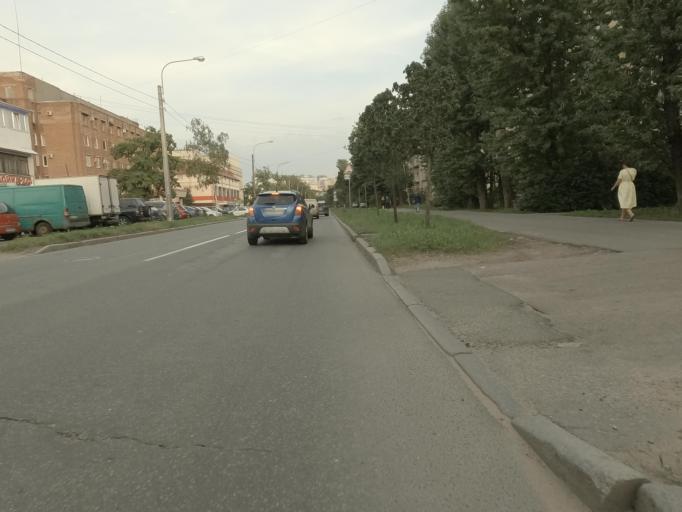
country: RU
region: St.-Petersburg
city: Dachnoye
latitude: 59.8557
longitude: 30.2623
